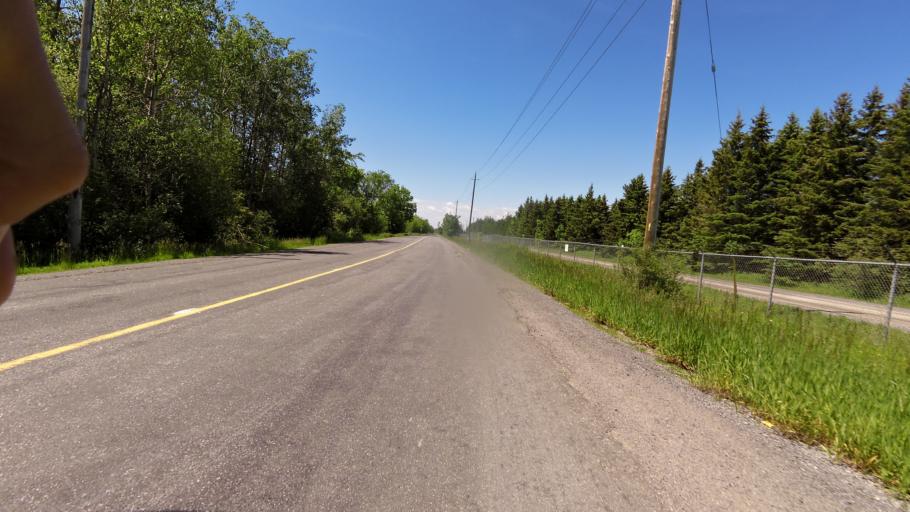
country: CA
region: Ontario
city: Bells Corners
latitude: 45.3575
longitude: -75.9121
